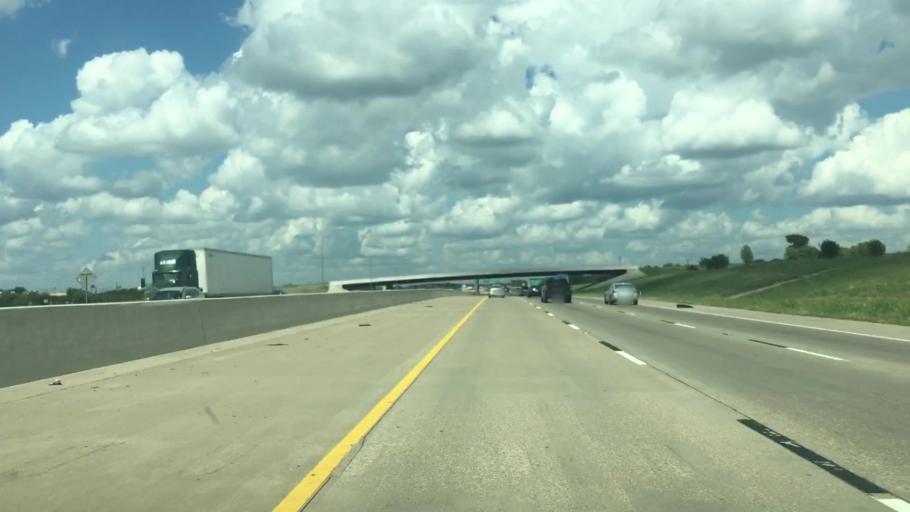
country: US
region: Texas
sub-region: Hill County
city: Hillsboro
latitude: 31.9971
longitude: -97.1000
